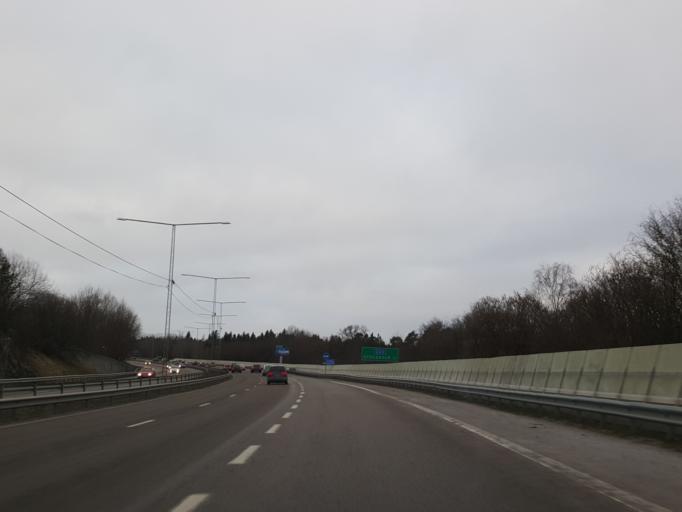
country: SE
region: Stockholm
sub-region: Lidingo
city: Brevik
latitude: 59.3160
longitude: 18.2080
